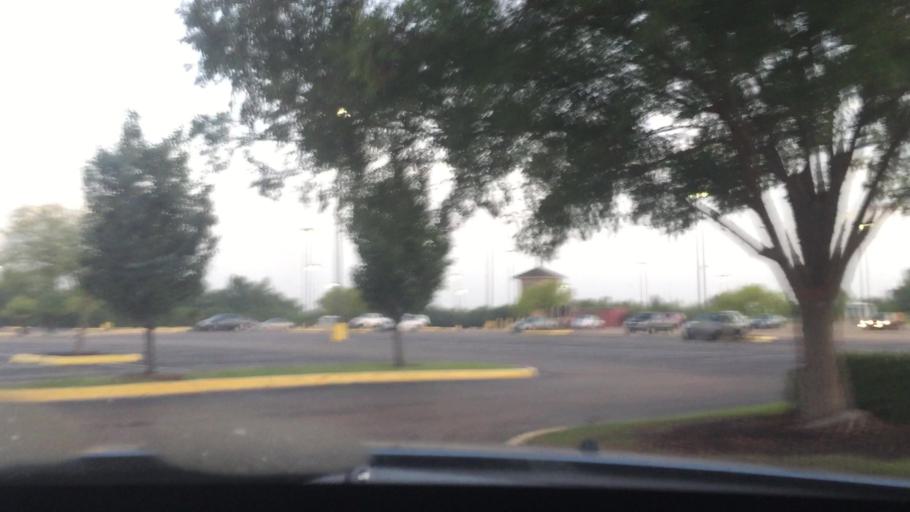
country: US
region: Louisiana
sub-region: West Baton Rouge Parish
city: Port Allen
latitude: 30.4605
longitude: -91.1903
